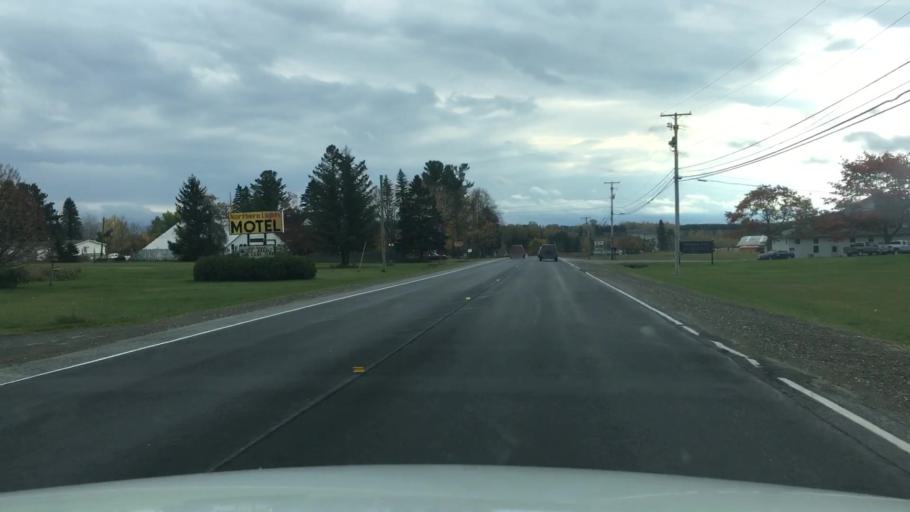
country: US
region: Maine
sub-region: Aroostook County
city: Presque Isle
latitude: 46.6550
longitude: -68.0054
